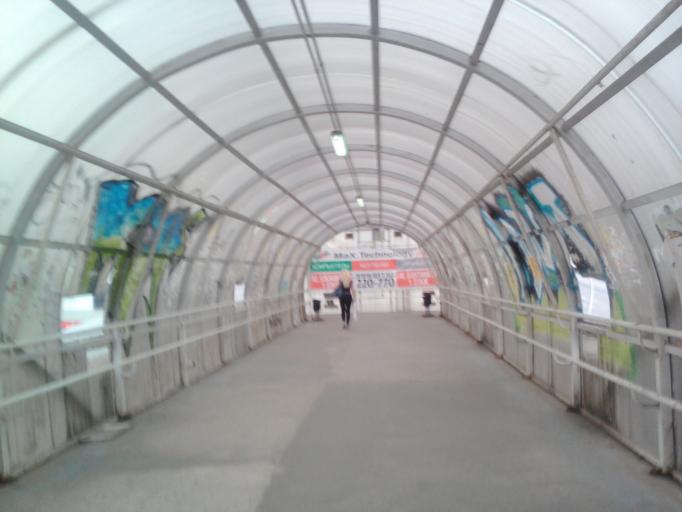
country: RU
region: Kursk
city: Kursk
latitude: 51.7271
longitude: 36.1855
